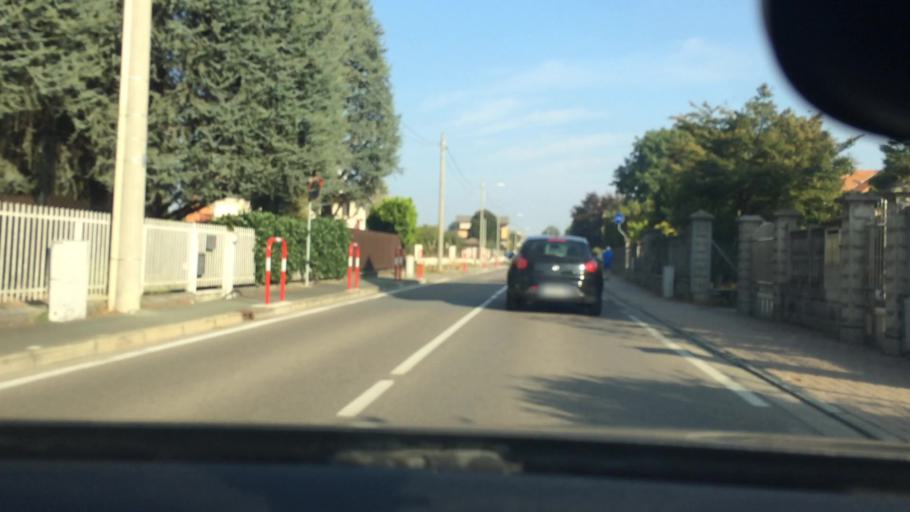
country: IT
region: Lombardy
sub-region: Provincia di Varese
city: Uboldo
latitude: 45.6183
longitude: 9.0031
